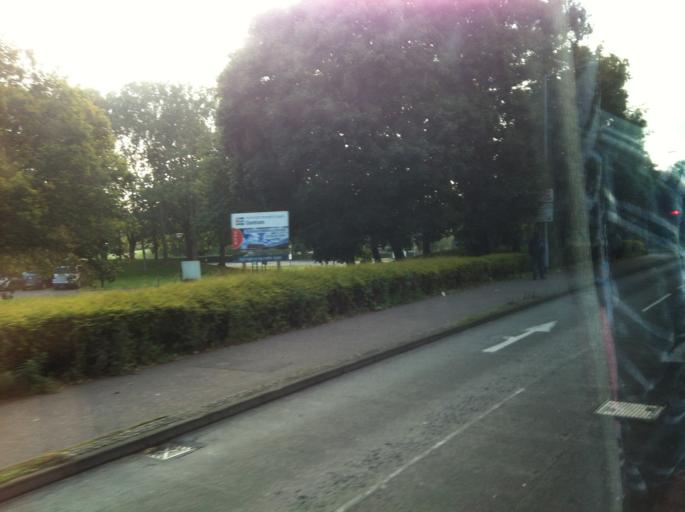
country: GB
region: England
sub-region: Norfolk
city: Bowthorpe
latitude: 52.6243
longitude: 1.2218
